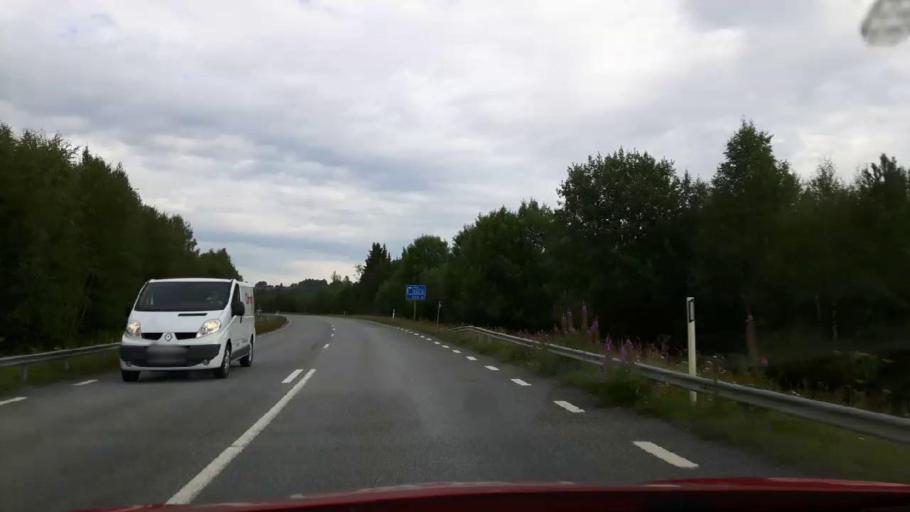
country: SE
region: Jaemtland
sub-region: Stroemsunds Kommun
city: Stroemsund
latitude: 63.5447
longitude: 15.3708
